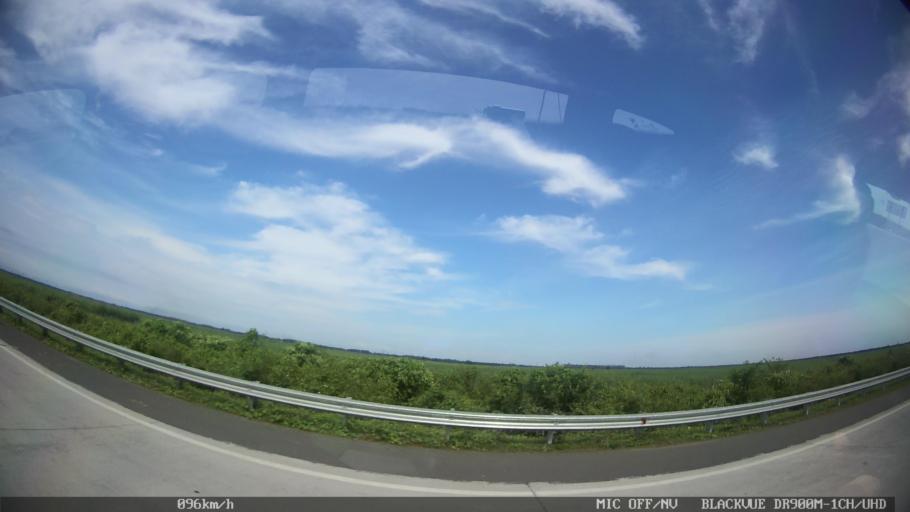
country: ID
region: North Sumatra
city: Binjai
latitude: 3.6750
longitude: 98.5355
